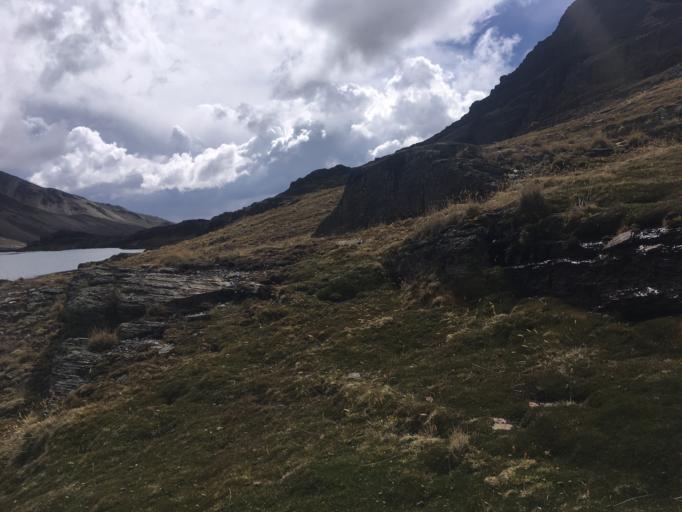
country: BO
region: La Paz
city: La Paz
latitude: -16.3925
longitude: -67.9654
